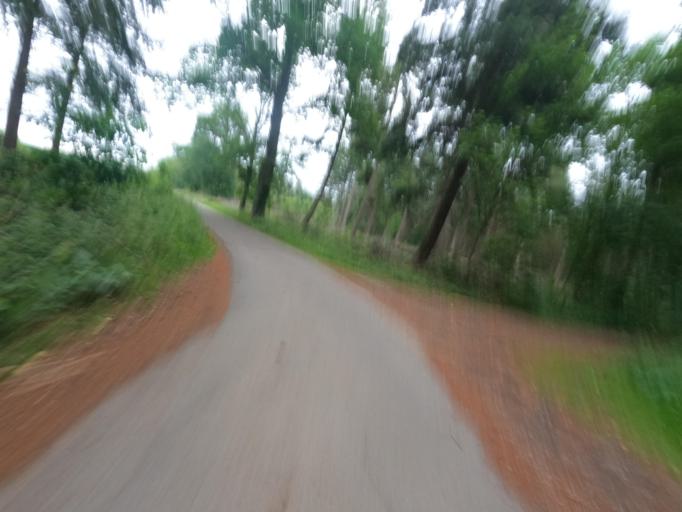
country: DE
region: North Rhine-Westphalia
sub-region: Regierungsbezirk Koln
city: Wassenberg
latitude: 51.1235
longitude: 6.1213
